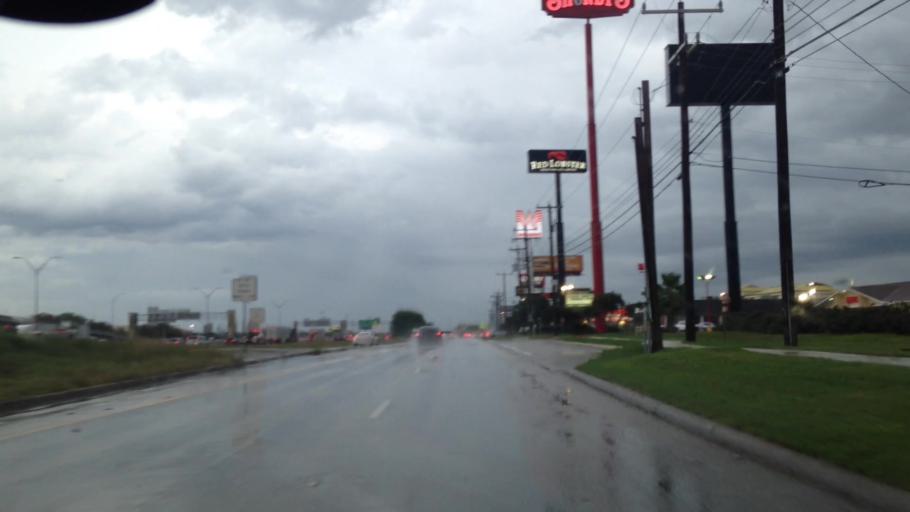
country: US
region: Texas
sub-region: Bexar County
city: Windcrest
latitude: 29.5114
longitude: -98.3969
